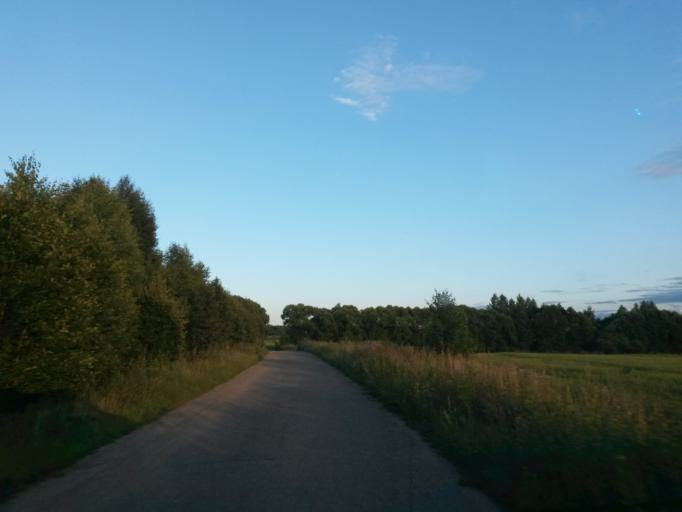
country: RU
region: Jaroslavl
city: Gavrilov-Yam
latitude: 57.3377
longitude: 40.0376
